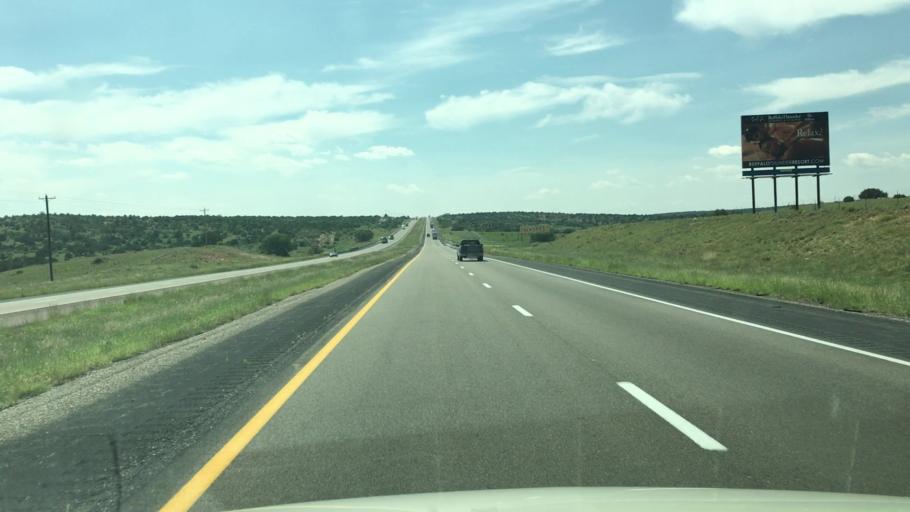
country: US
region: New Mexico
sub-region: San Miguel County
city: Las Vegas
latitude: 34.9920
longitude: -105.3021
